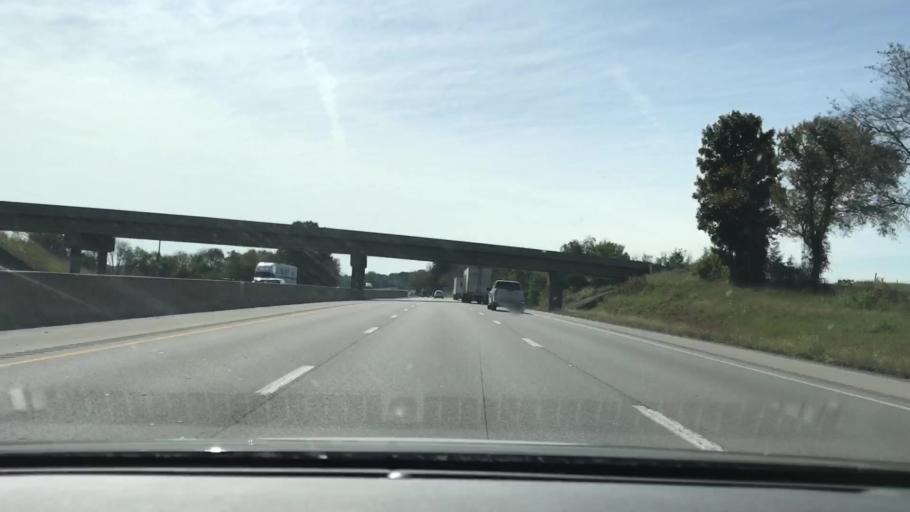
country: US
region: Kentucky
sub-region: Simpson County
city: Franklin
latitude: 36.7368
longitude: -86.5077
